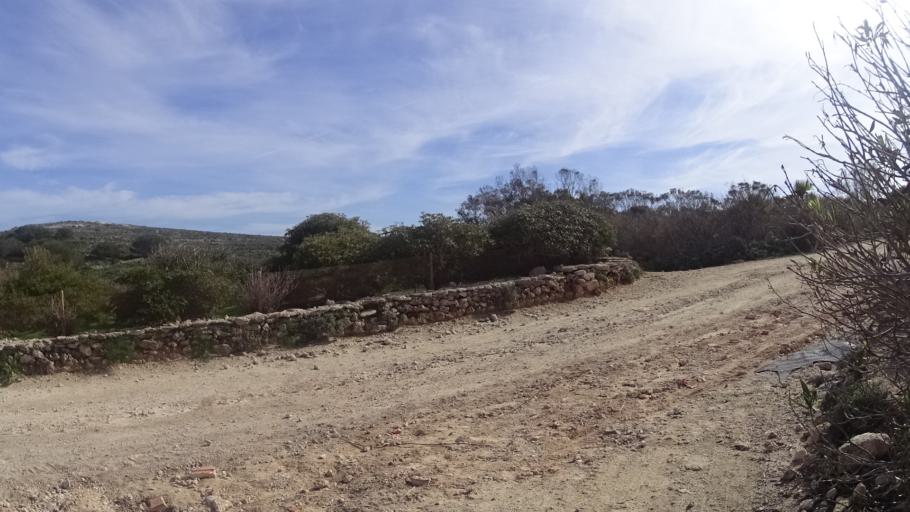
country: MT
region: Il-Qala
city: Qala
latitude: 36.0161
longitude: 14.3286
